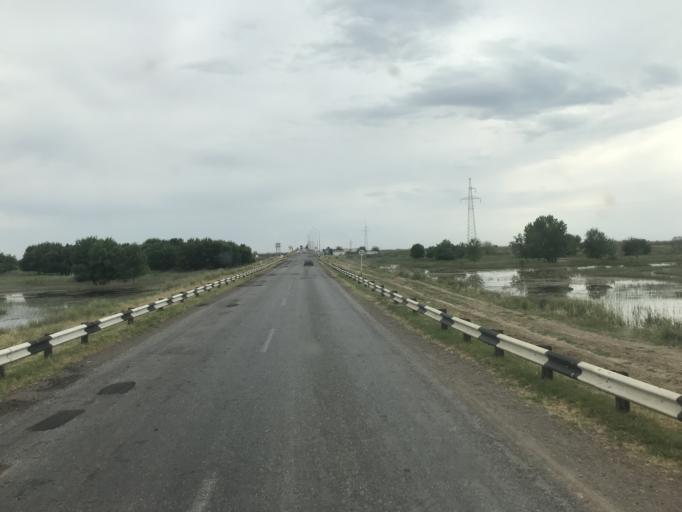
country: KZ
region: Ongtustik Qazaqstan
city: Ilyich
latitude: 41.0329
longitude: 68.5239
